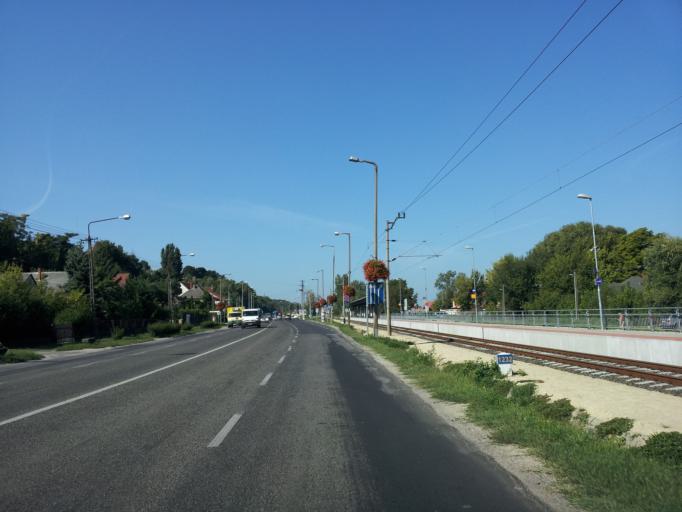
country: HU
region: Somogy
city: Zamardi
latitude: 46.8807
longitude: 17.9480
